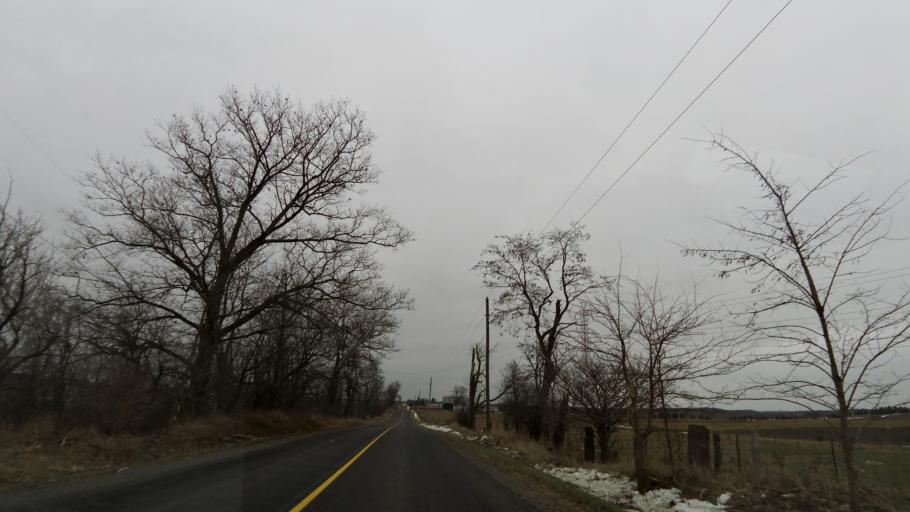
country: CA
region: Ontario
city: Brantford
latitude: 43.1077
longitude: -80.1888
